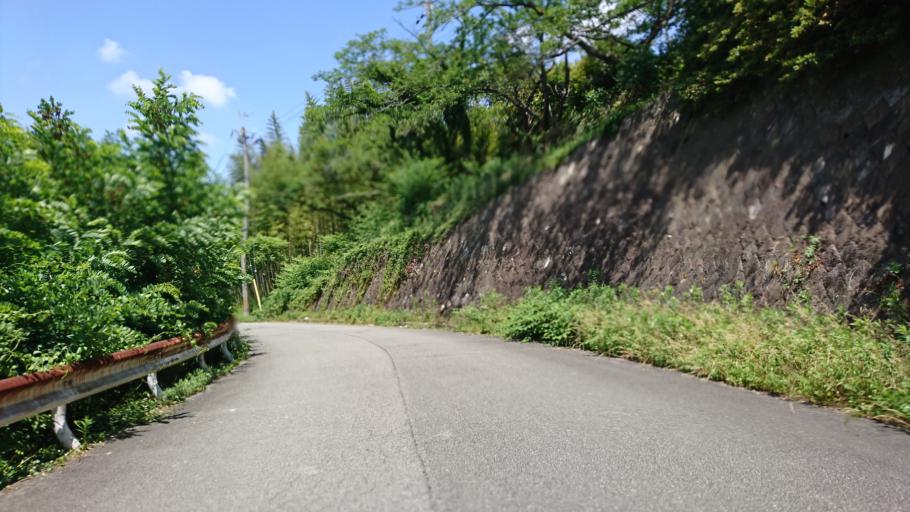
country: JP
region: Hyogo
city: Kakogawacho-honmachi
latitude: 34.8028
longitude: 134.7911
